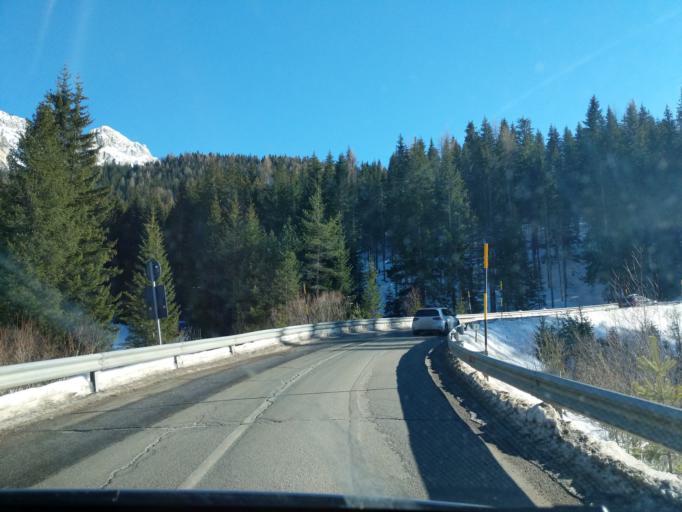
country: IT
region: Veneto
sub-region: Provincia di Belluno
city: Livinallongo del Col di Lana
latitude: 46.5526
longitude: 11.9689
